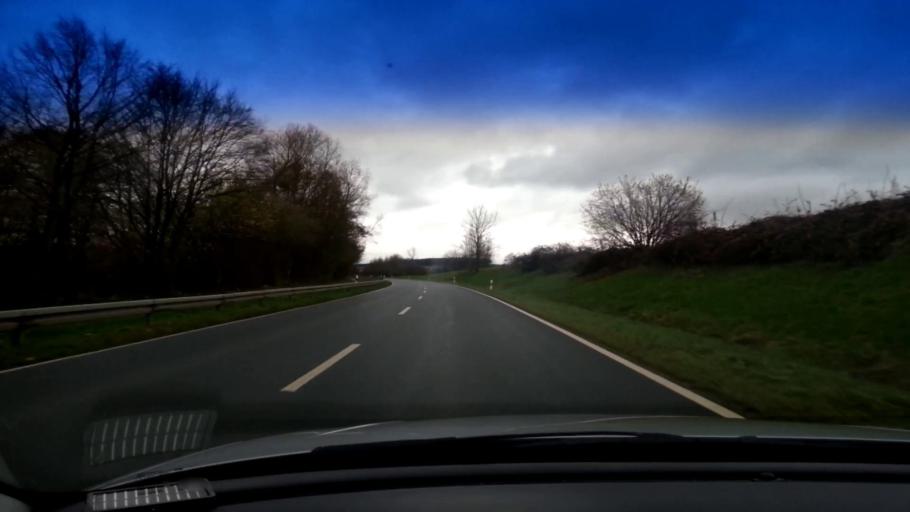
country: DE
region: Bavaria
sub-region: Upper Franconia
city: Ebensfeld
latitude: 50.0401
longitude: 10.9999
